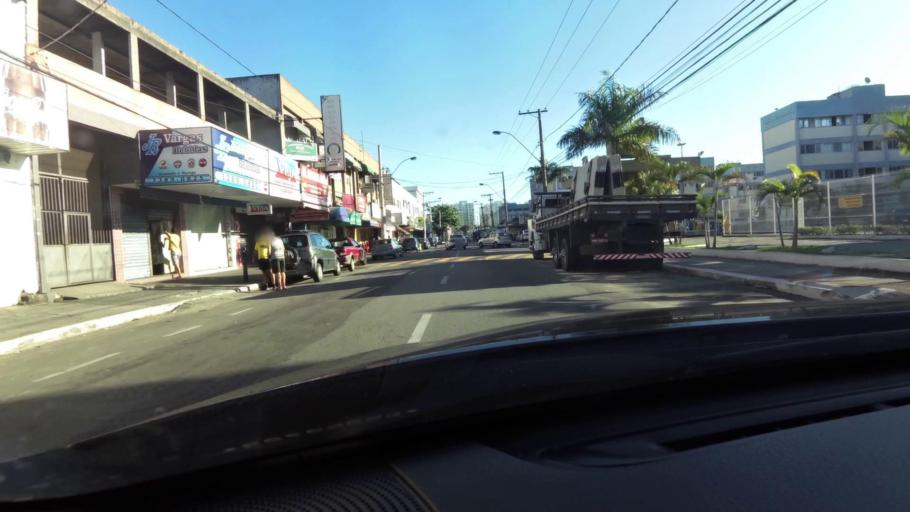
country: BR
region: Espirito Santo
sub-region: Vila Velha
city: Vila Velha
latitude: -20.3616
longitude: -40.3003
